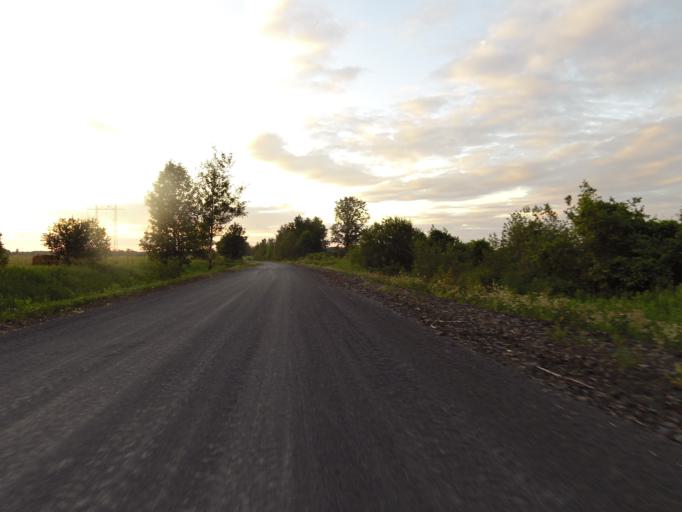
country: CA
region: Ontario
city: Arnprior
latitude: 45.3950
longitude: -76.3222
